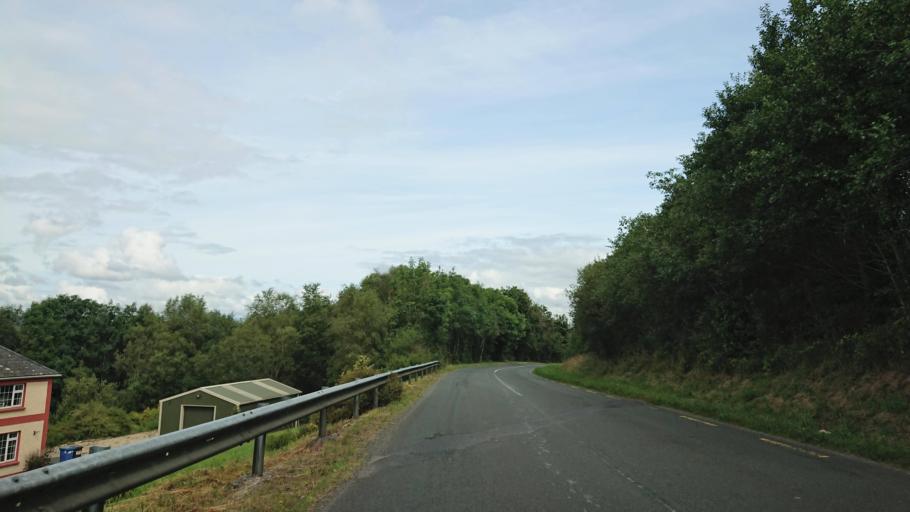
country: IE
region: Connaught
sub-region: County Leitrim
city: Carrick-on-Shannon
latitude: 54.0636
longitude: -8.0372
